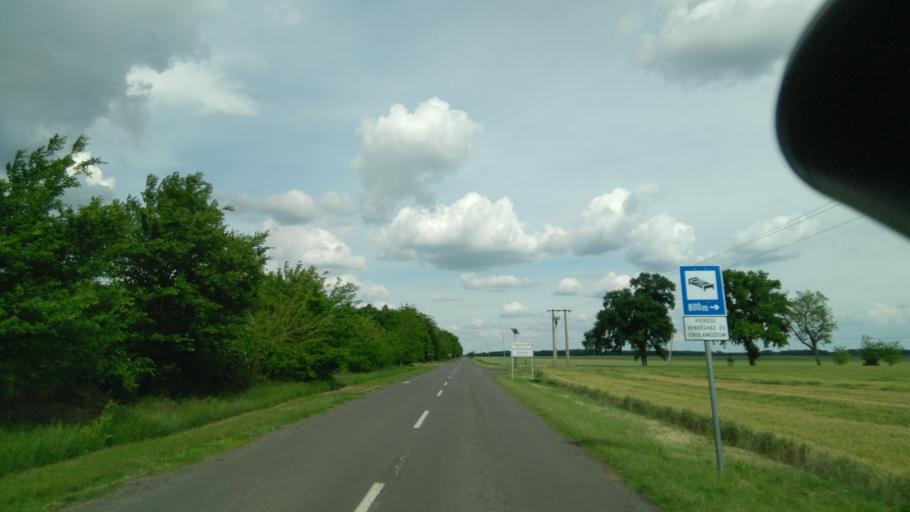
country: RO
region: Arad
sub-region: Comuna Peregu Mare
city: Peregu Mic
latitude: 46.3047
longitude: 20.9042
